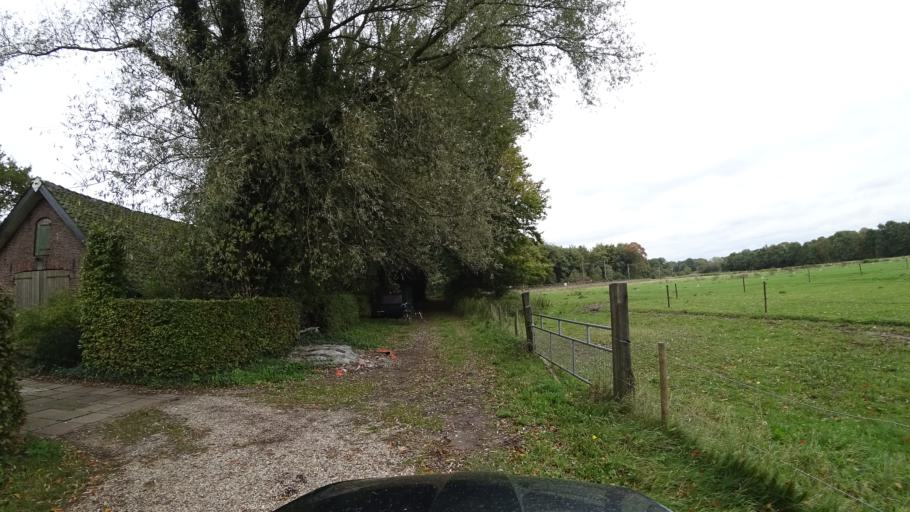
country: NL
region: Utrecht
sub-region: Gemeente De Bilt
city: De Bilt
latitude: 52.1205
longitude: 5.1706
